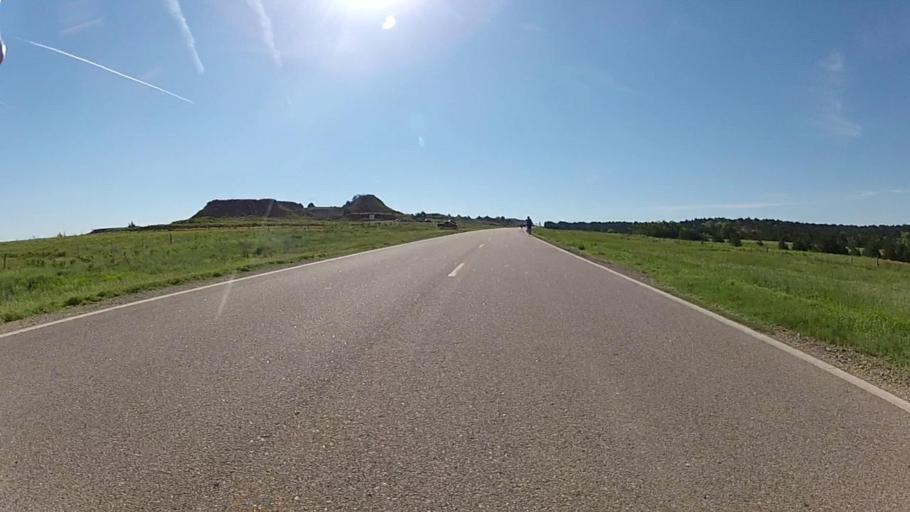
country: US
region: Kansas
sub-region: Barber County
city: Medicine Lodge
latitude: 37.2822
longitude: -98.7521
